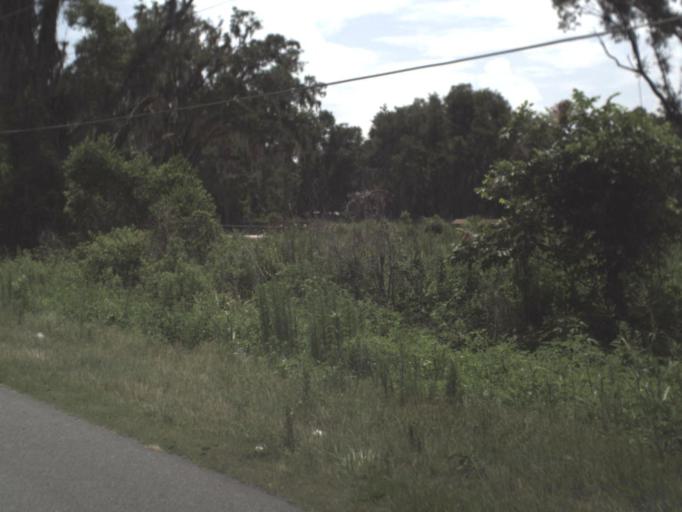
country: US
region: Florida
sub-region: Madison County
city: Madison
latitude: 30.4692
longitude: -83.3892
